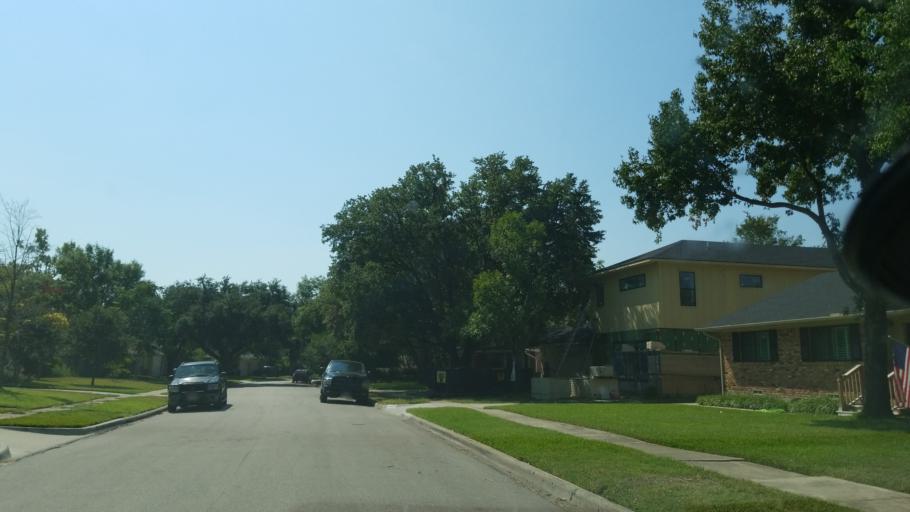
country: US
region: Texas
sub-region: Dallas County
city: Richardson
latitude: 32.8771
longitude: -96.7069
